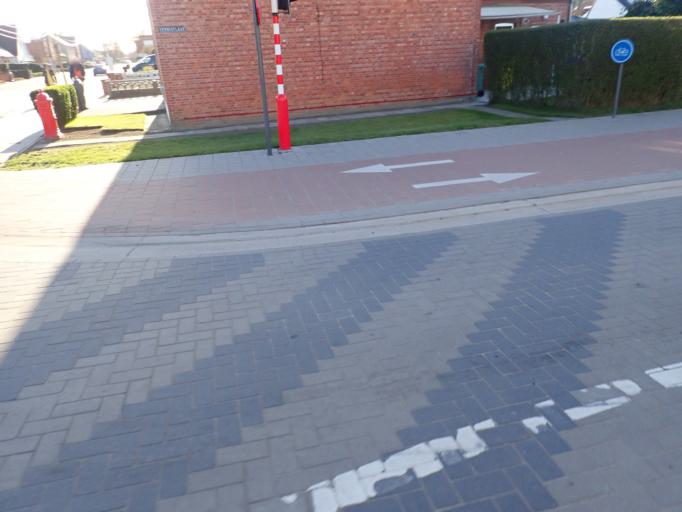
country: BE
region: Flanders
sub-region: Provincie Antwerpen
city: Herenthout
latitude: 51.1371
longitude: 4.7463
